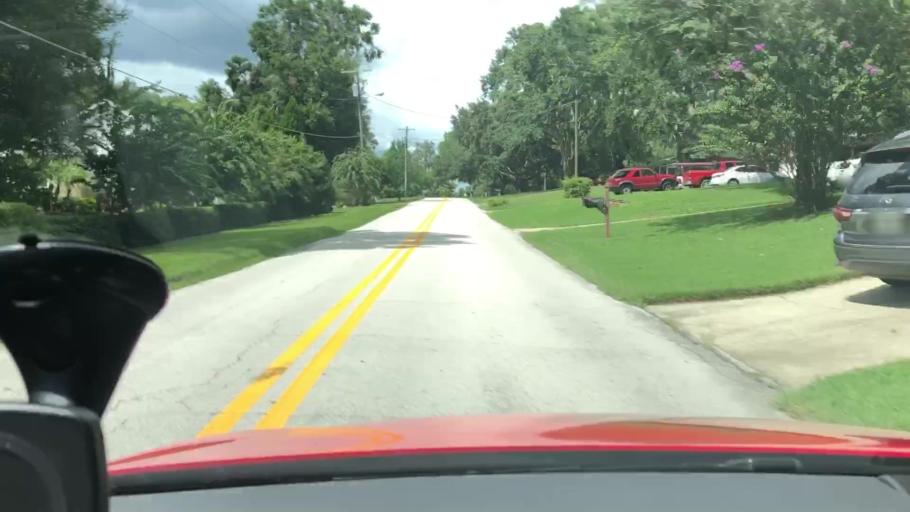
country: US
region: Florida
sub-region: Lake County
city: Mount Dora
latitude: 28.8313
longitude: -81.6587
